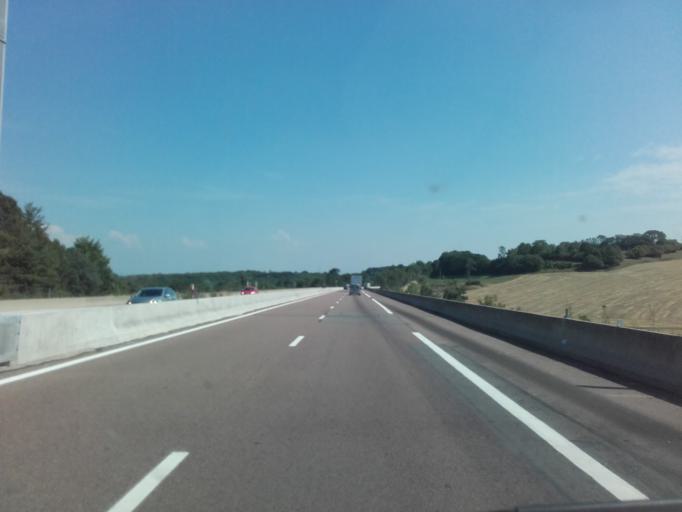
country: FR
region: Bourgogne
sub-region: Departement de la Cote-d'Or
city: Savigny-les-Beaune
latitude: 47.0967
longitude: 4.7464
